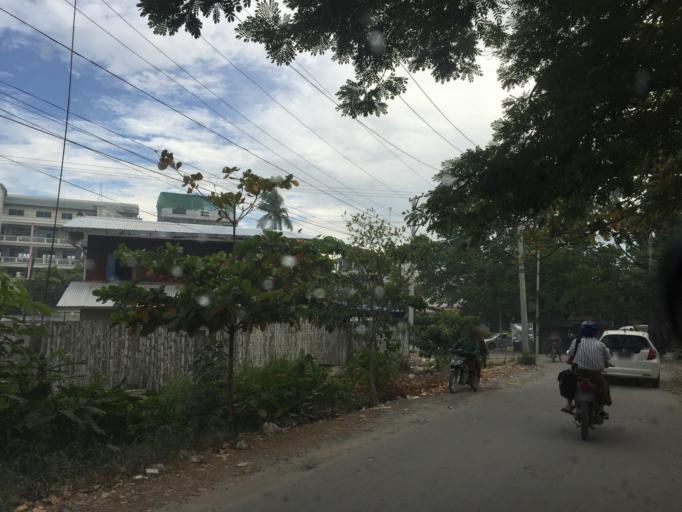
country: MM
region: Mandalay
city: Mandalay
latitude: 21.9721
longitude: 96.1093
